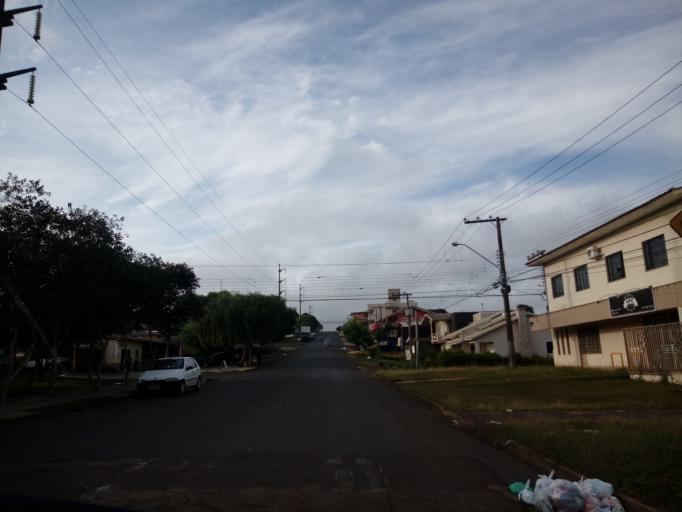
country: BR
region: Santa Catarina
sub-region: Chapeco
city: Chapeco
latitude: -27.0775
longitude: -52.6380
